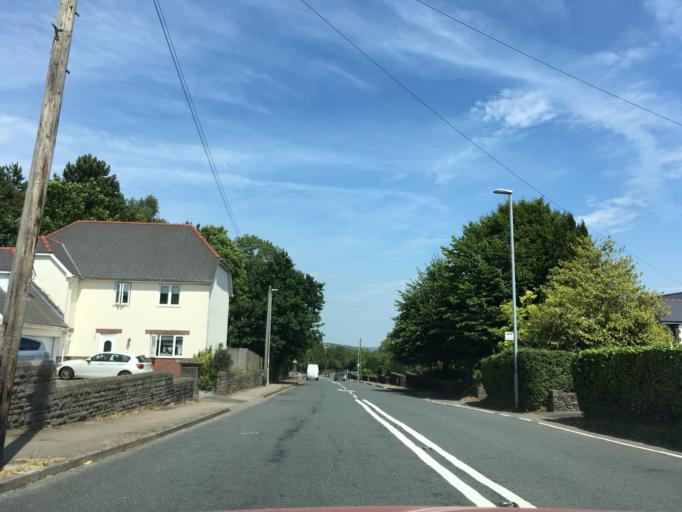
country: GB
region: Wales
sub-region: Newport
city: Caerleon
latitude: 51.5943
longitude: -2.9532
